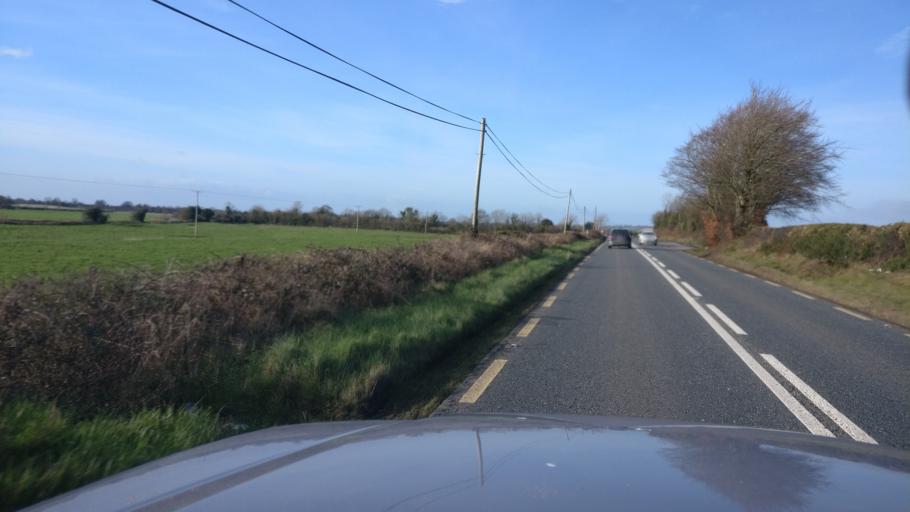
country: IE
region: Leinster
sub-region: Laois
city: Mountmellick
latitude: 53.1624
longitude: -7.3700
